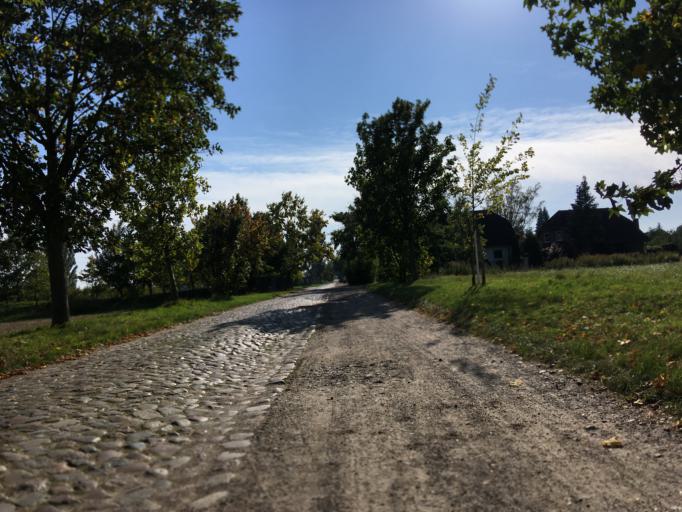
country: DE
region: Brandenburg
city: Altlandsberg
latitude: 52.5593
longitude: 13.7294
